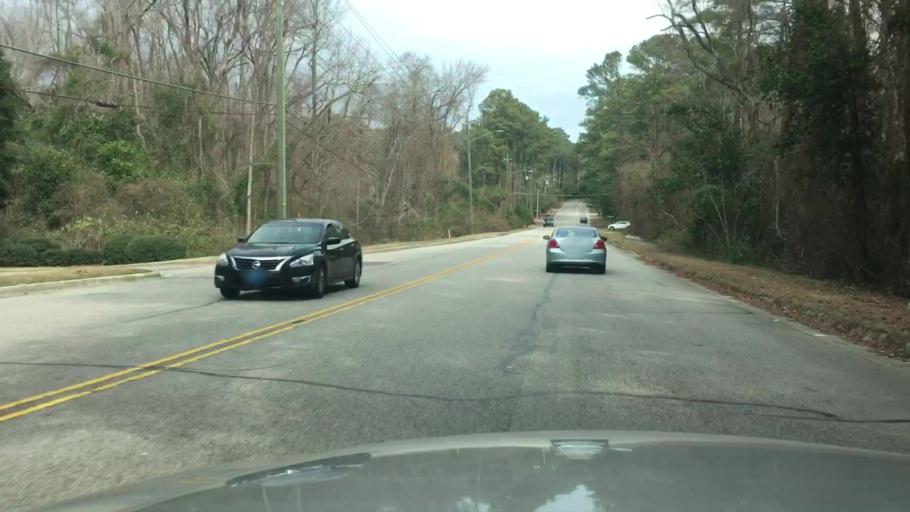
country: US
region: North Carolina
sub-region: Cumberland County
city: Fayetteville
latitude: 35.0495
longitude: -78.9145
